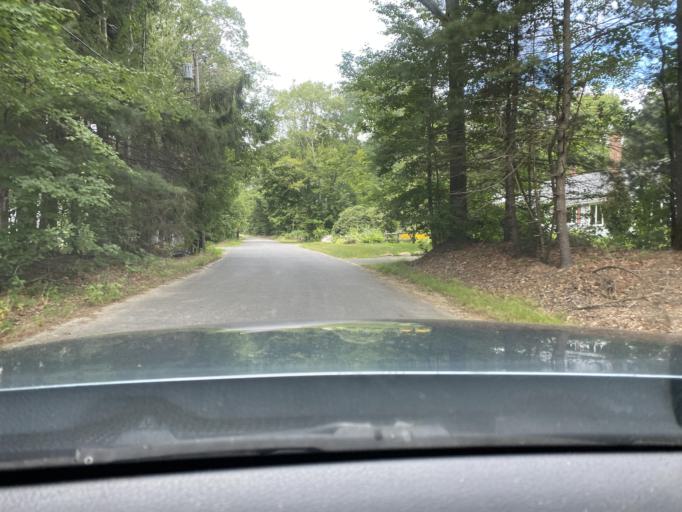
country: US
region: Massachusetts
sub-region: Norfolk County
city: Millis-Clicquot
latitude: 42.1803
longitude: -71.3324
